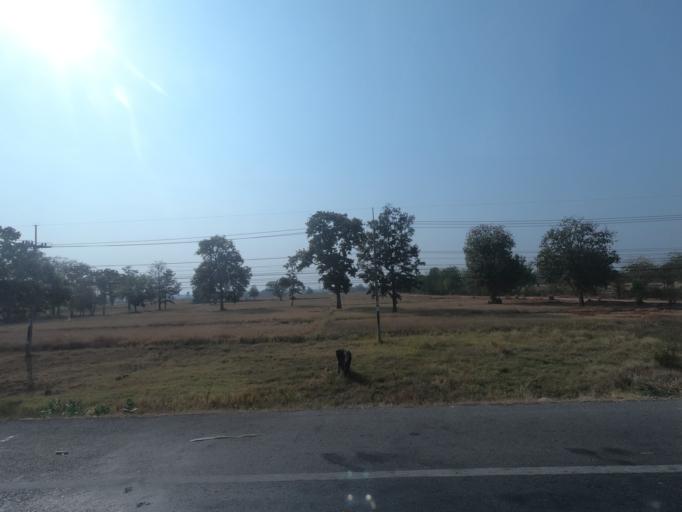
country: TH
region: Khon Kaen
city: Ban Haet
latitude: 16.1558
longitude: 102.7528
